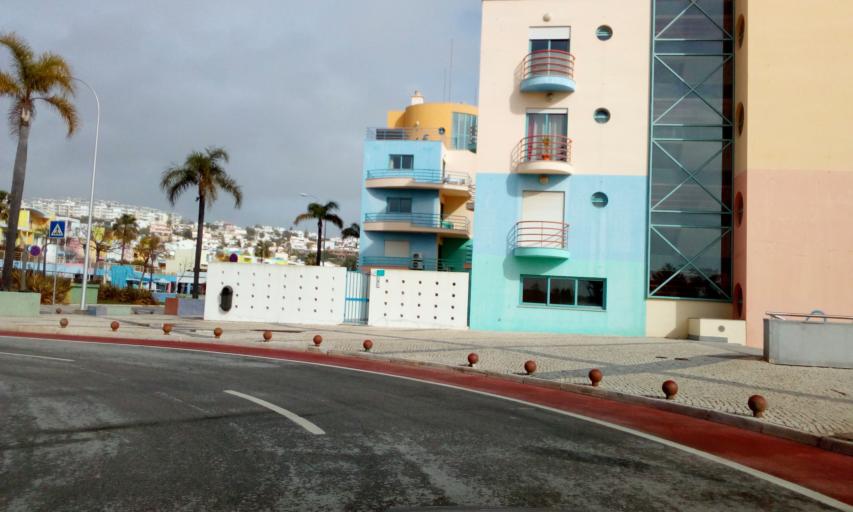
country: PT
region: Faro
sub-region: Albufeira
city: Albufeira
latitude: 37.0852
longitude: -8.2692
